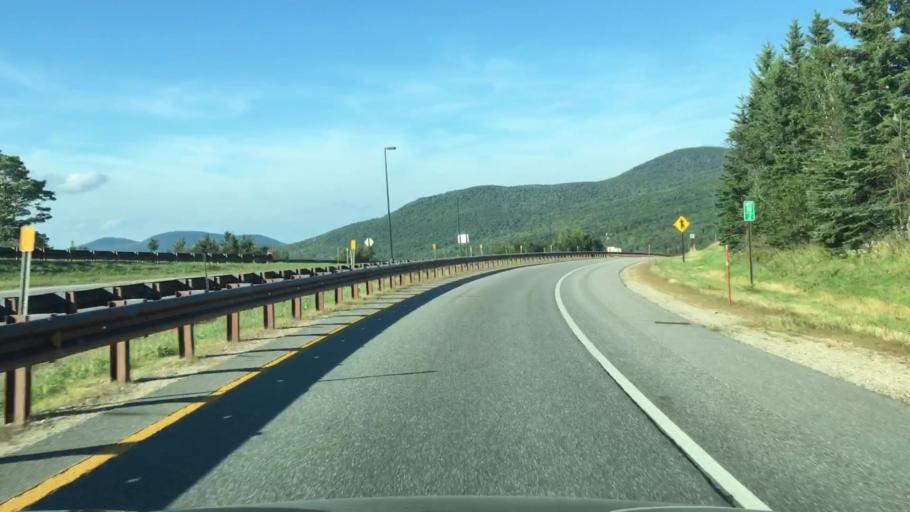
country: US
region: New Hampshire
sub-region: Grafton County
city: Deerfield
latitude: 44.1802
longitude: -71.6913
